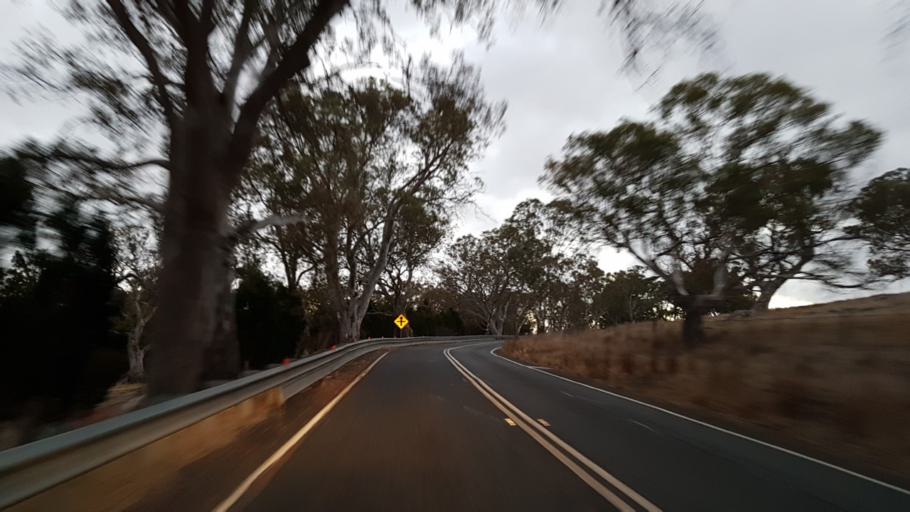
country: AU
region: South Australia
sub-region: Mount Barker
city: Nairne
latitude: -35.0326
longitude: 138.9534
